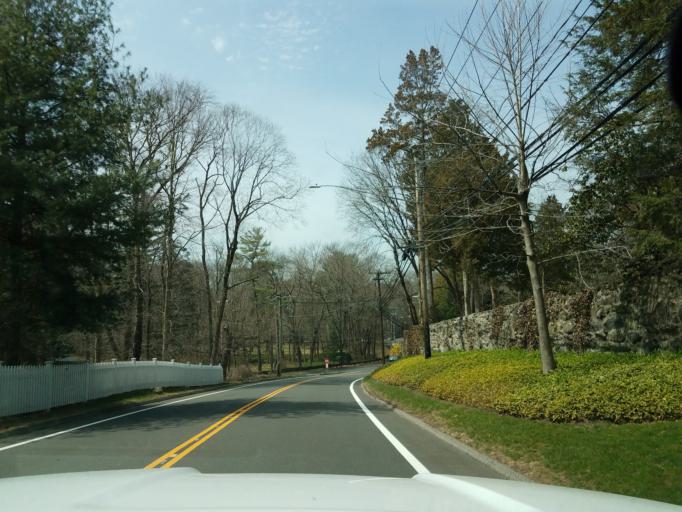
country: US
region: Connecticut
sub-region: Fairfield County
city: Greenwich
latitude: 41.0310
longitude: -73.6373
